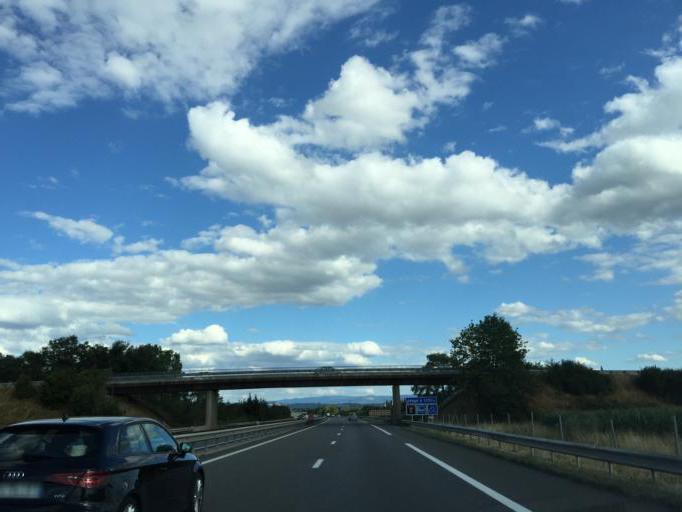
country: FR
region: Rhone-Alpes
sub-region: Departement de la Loire
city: Saint-Cyprien
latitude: 45.5663
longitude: 4.2294
